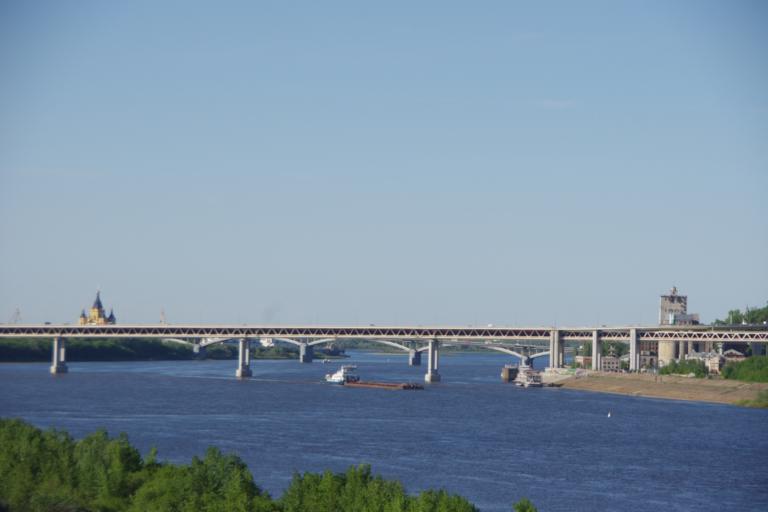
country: RU
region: Nizjnij Novgorod
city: Nizhniy Novgorod
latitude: 56.2988
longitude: 43.9558
